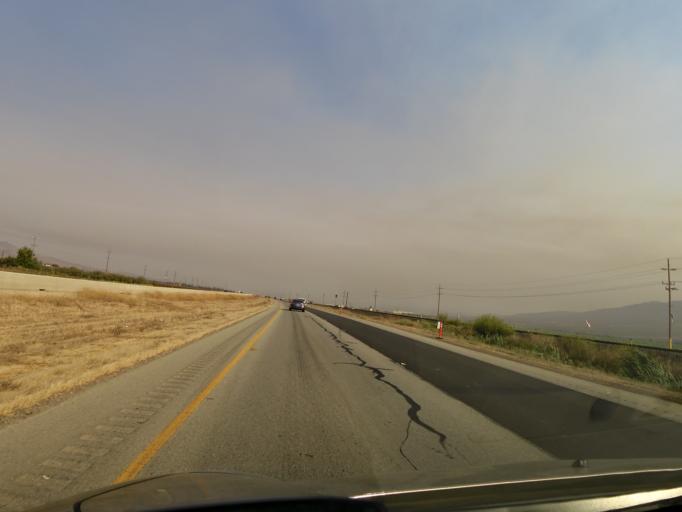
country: US
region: California
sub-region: Monterey County
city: Gonzales
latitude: 36.4850
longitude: -121.4193
